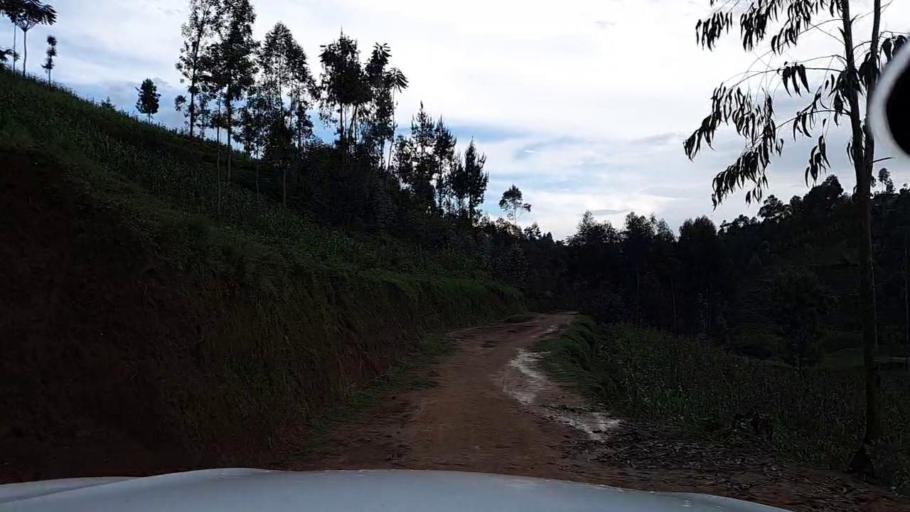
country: BI
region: Kayanza
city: Kayanza
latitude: -2.7747
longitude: 29.4470
